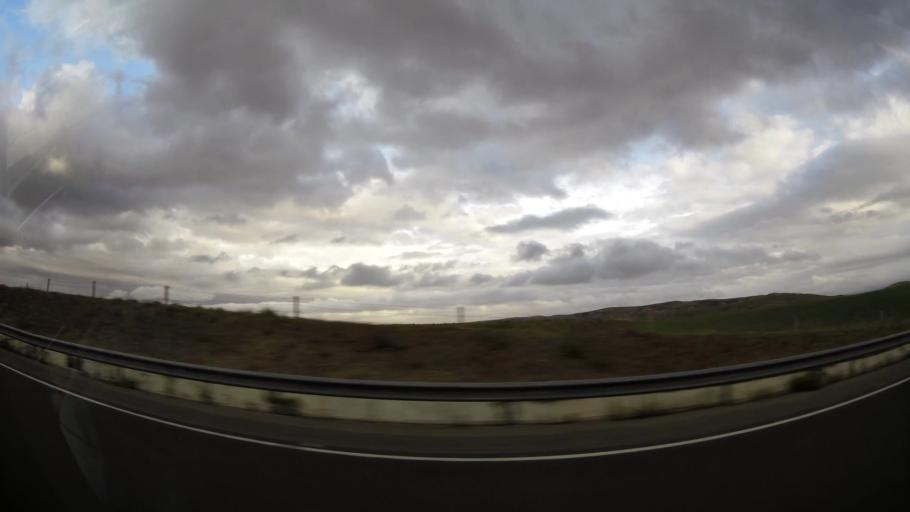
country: MA
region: Taza-Al Hoceima-Taounate
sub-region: Taza
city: Taza
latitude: 34.2600
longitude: -3.8498
